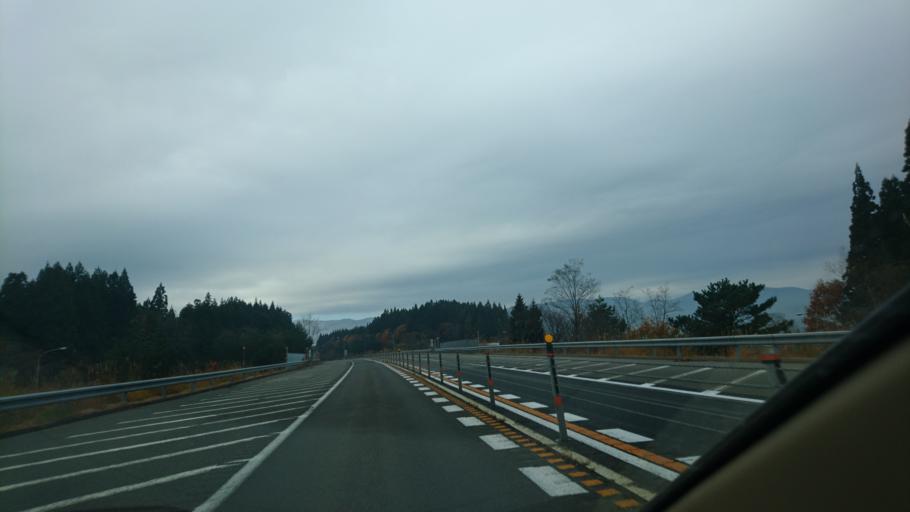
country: JP
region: Iwate
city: Kitakami
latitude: 39.2914
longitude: 140.9856
